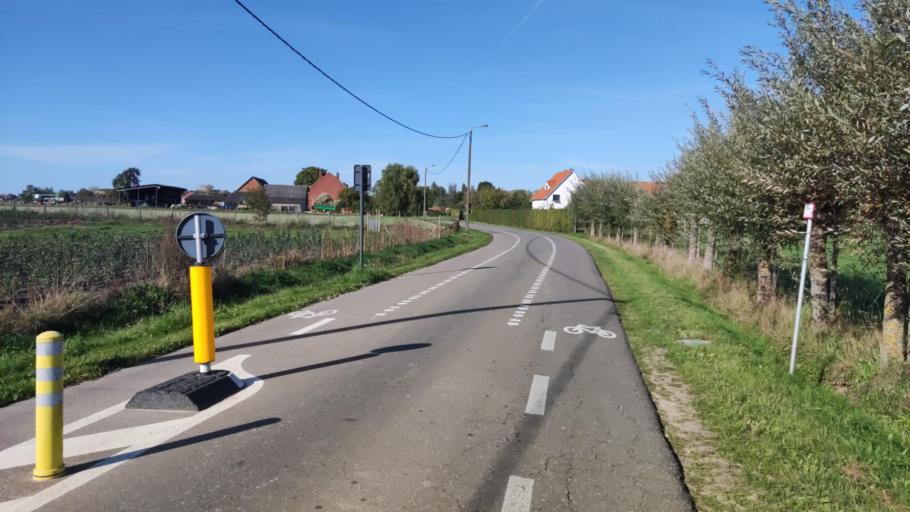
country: BE
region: Flanders
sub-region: Provincie Limburg
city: Alken
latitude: 50.9209
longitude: 5.2685
